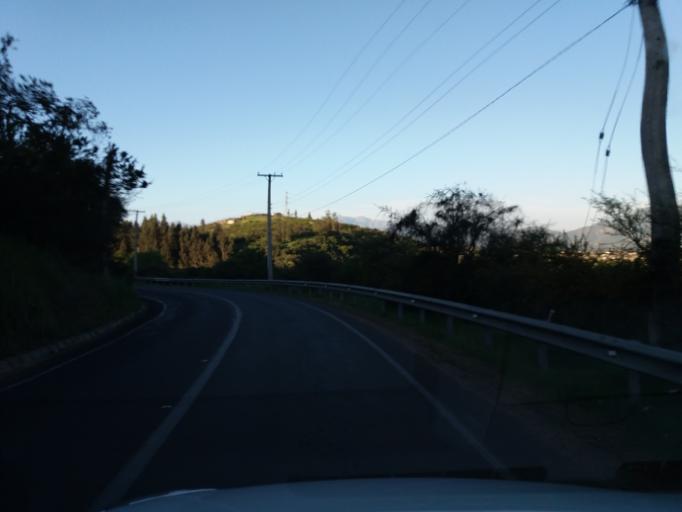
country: CL
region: Valparaiso
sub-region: Provincia de Quillota
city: Quillota
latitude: -32.8903
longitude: -71.2823
